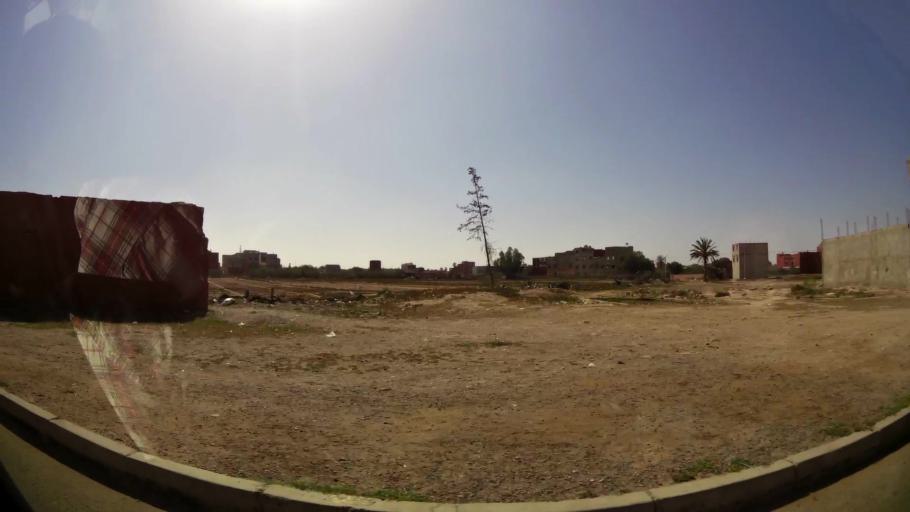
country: MA
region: Souss-Massa-Draa
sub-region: Inezgane-Ait Mellou
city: Inezgane
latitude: 30.3282
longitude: -9.5233
